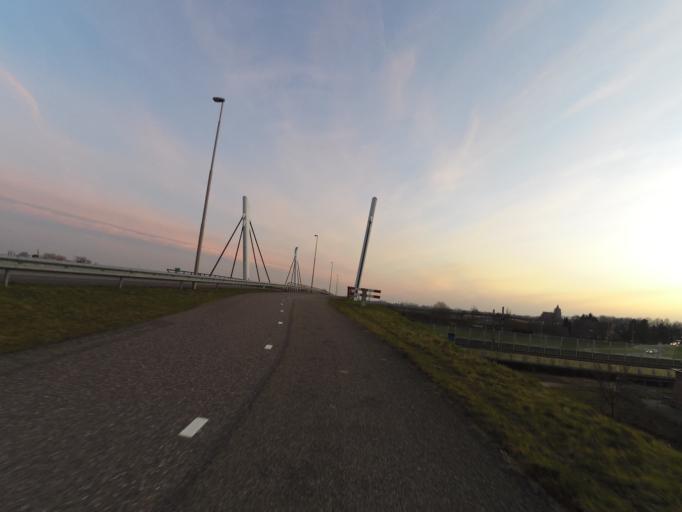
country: NL
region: Gelderland
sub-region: Gemeente Zevenaar
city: Zevenaar
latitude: 51.9192
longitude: 6.0904
